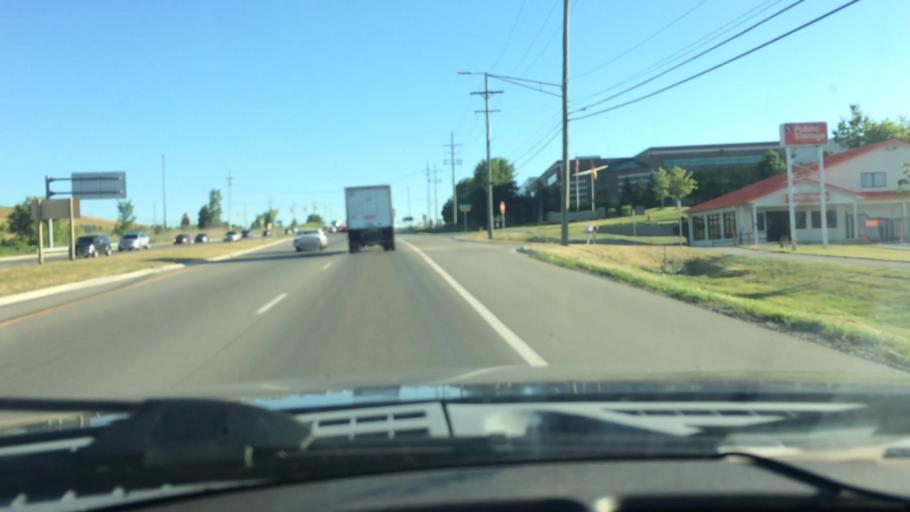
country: US
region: Michigan
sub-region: Oakland County
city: Auburn Hills
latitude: 42.7005
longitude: -83.2422
